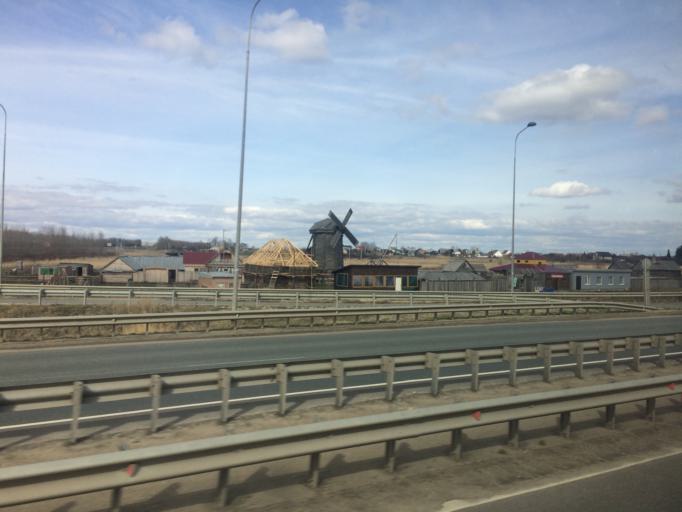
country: RU
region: Tatarstan
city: Nizhniye Vyazovyye
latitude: 55.7235
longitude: 48.5393
